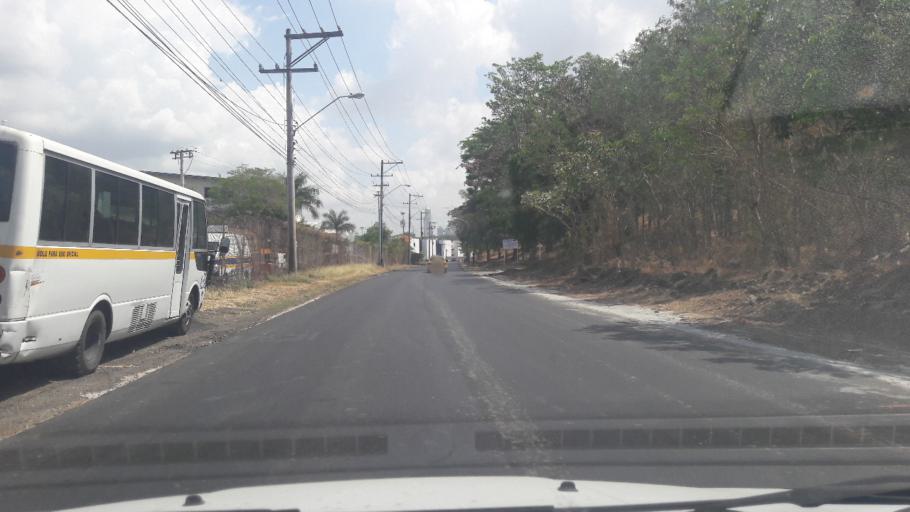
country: PA
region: Panama
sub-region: Distrito de Panama
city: Ancon
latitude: 8.9727
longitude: -79.5465
